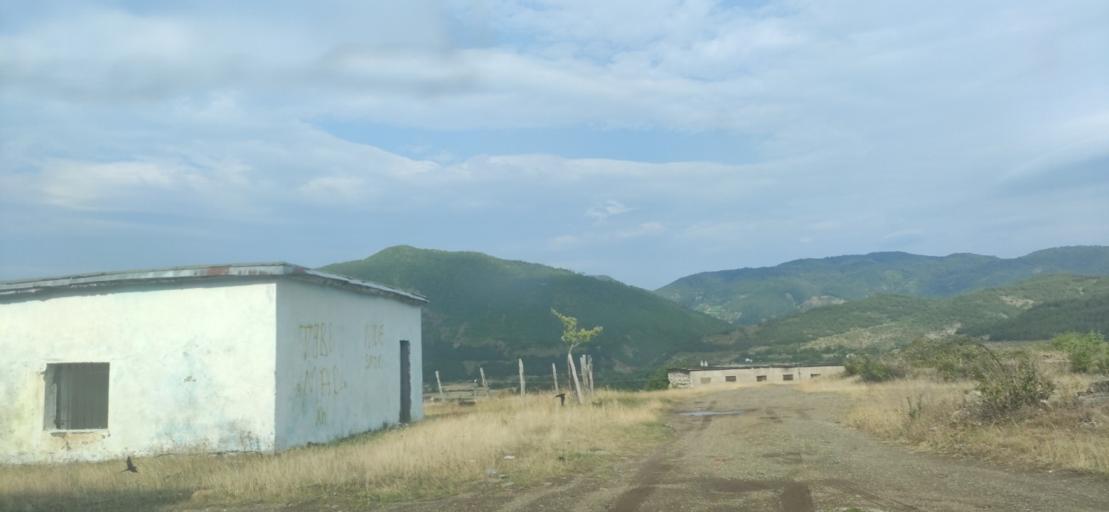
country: AL
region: Shkoder
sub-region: Rrethi i Pukes
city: Iballe
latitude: 42.1873
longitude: 20.0045
